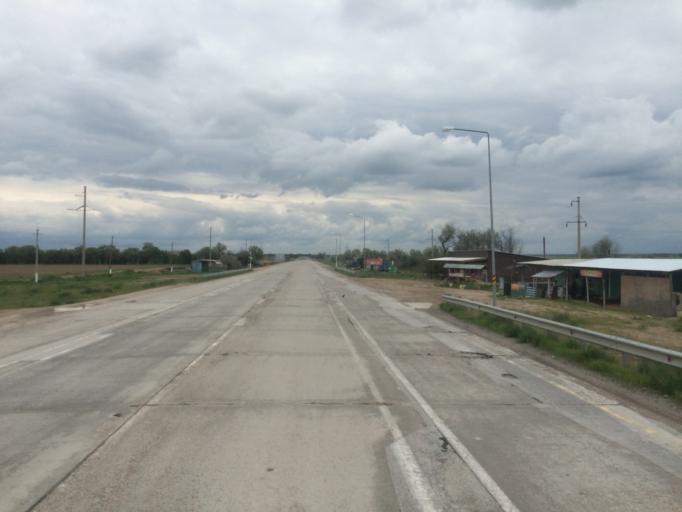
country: KG
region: Chuy
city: Sokuluk
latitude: 43.2719
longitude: 74.2386
